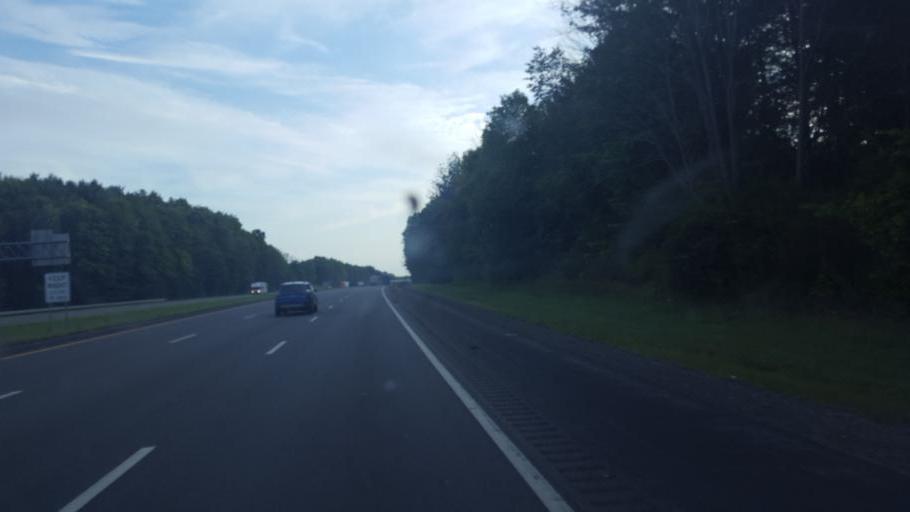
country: US
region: Ohio
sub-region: Sandusky County
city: Bellville
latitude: 40.6364
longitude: -82.5529
